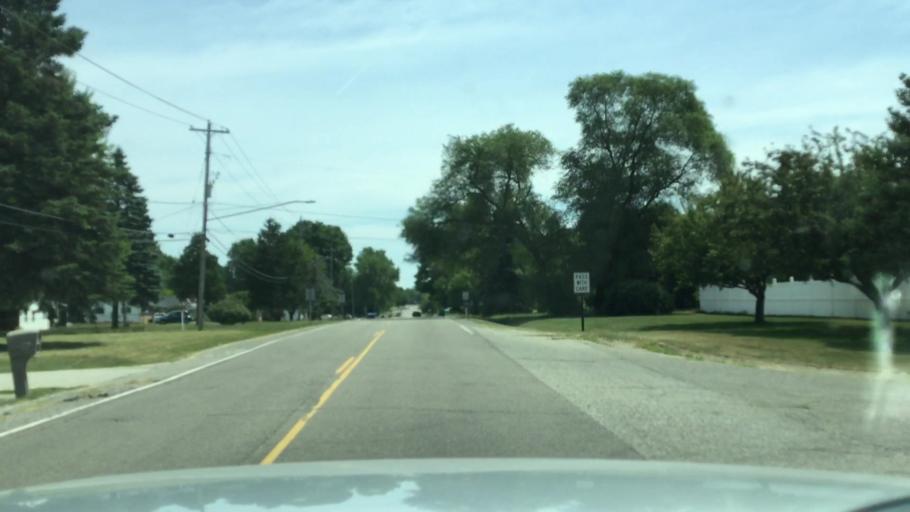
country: US
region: Michigan
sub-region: Genesee County
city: Swartz Creek
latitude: 43.0161
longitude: -83.8036
